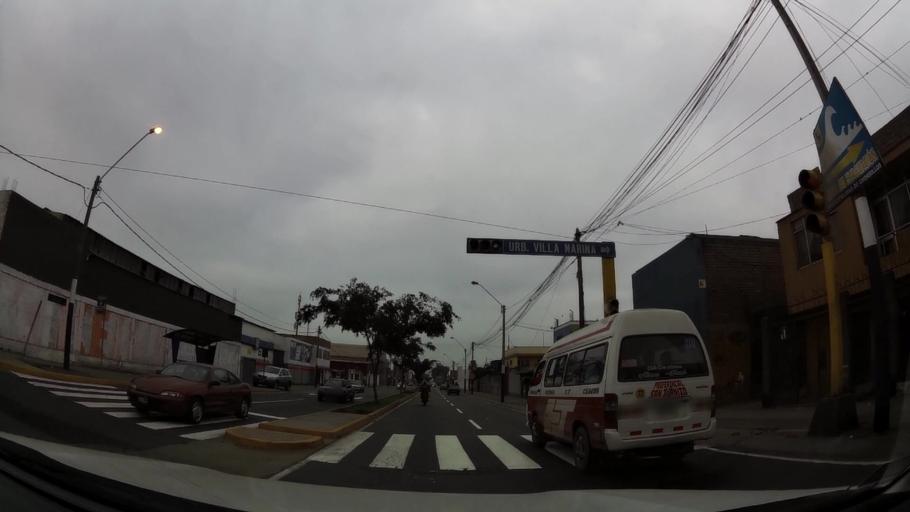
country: PE
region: Lima
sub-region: Lima
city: Surco
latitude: -12.1927
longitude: -77.0082
